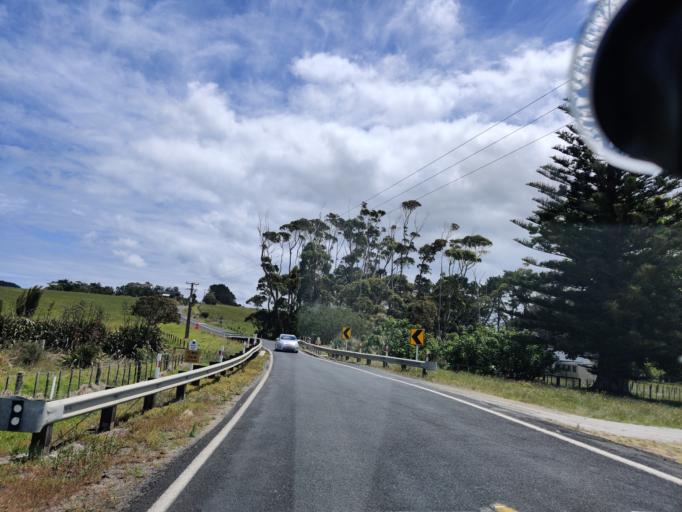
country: NZ
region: Northland
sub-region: Far North District
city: Kaitaia
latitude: -34.7084
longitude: 173.0343
